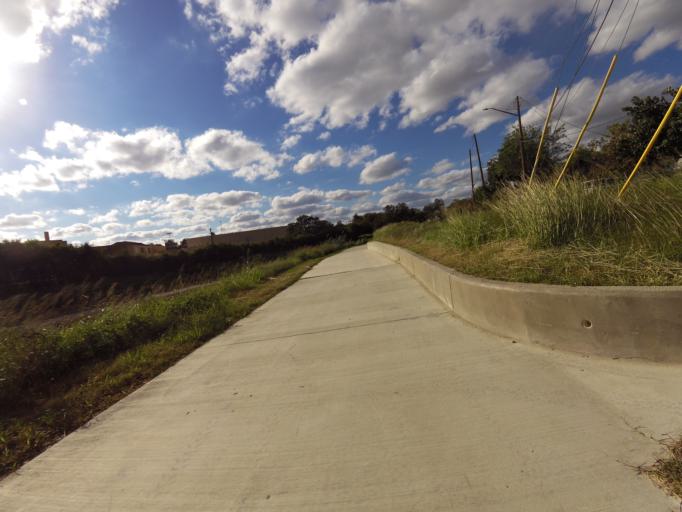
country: US
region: Texas
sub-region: Bexar County
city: San Antonio
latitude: 29.4000
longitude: -98.5053
